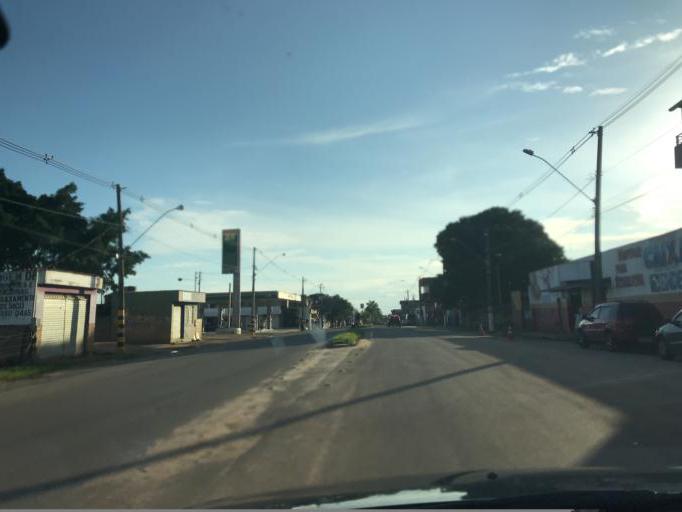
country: BR
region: Minas Gerais
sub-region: Tres Coracoes
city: Tres Coracoes
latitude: -21.6905
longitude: -45.2386
